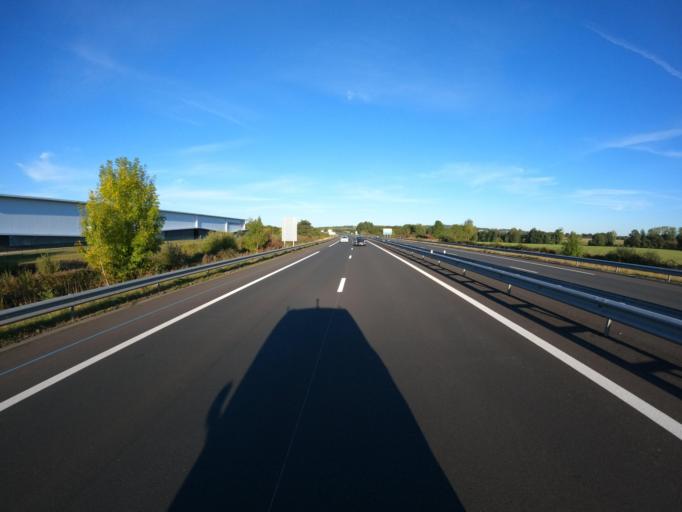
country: FR
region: Pays de la Loire
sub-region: Departement de la Vendee
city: Beaurepaire
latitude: 46.8971
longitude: -1.0710
